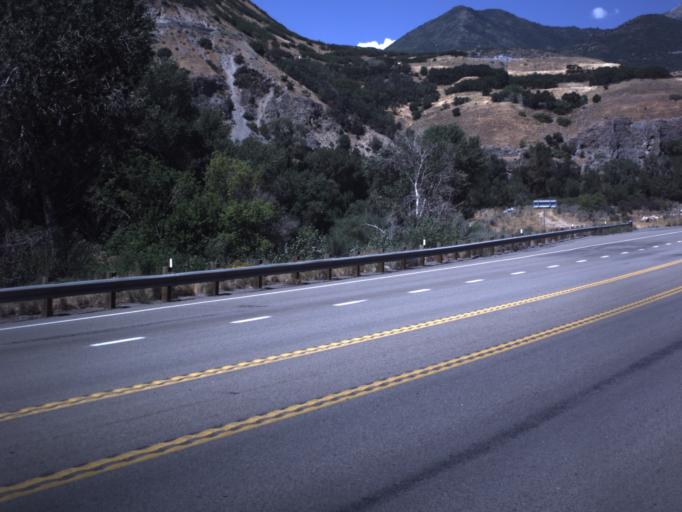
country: US
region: Utah
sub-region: Utah County
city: Orem
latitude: 40.3187
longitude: -111.6494
